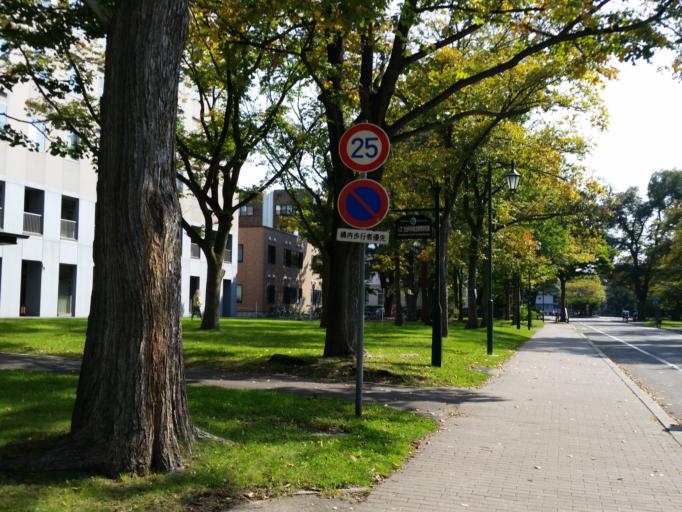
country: JP
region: Hokkaido
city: Sapporo
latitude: 43.0724
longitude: 141.3427
